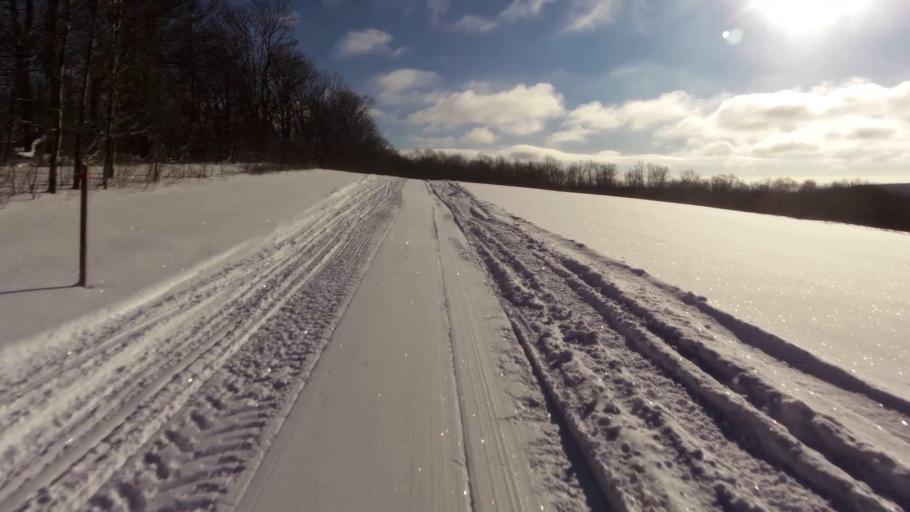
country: US
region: New York
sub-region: Chautauqua County
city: Falconer
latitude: 42.2606
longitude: -79.1759
